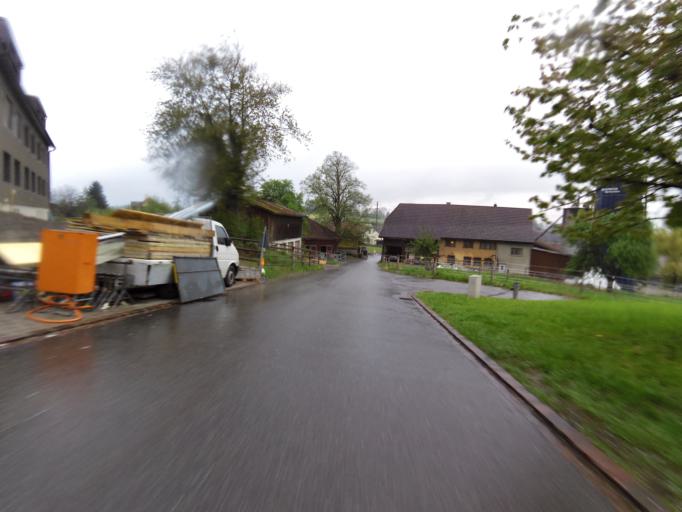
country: CH
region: Thurgau
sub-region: Frauenfeld District
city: Gachnang
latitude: 47.5526
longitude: 8.8619
